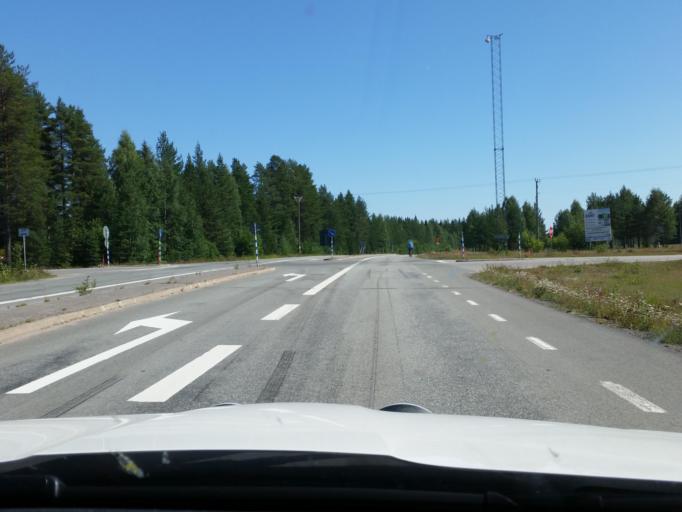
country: SE
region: Norrbotten
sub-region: Alvsbyns Kommun
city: AElvsbyn
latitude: 65.6715
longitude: 20.9483
